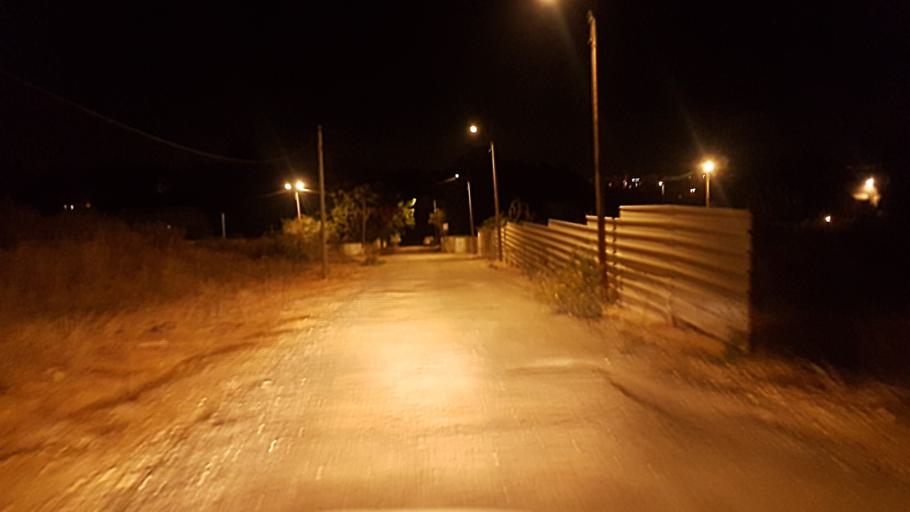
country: IL
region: Central District
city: Hod HaSharon
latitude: 32.1589
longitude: 34.8728
